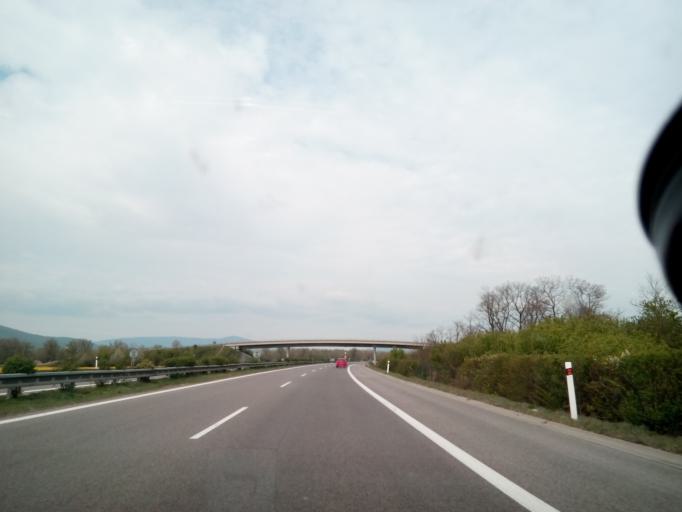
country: SK
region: Trenciansky
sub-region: Okres Nove Mesto nad Vahom
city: Nove Mesto nad Vahom
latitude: 48.7357
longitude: 17.8645
